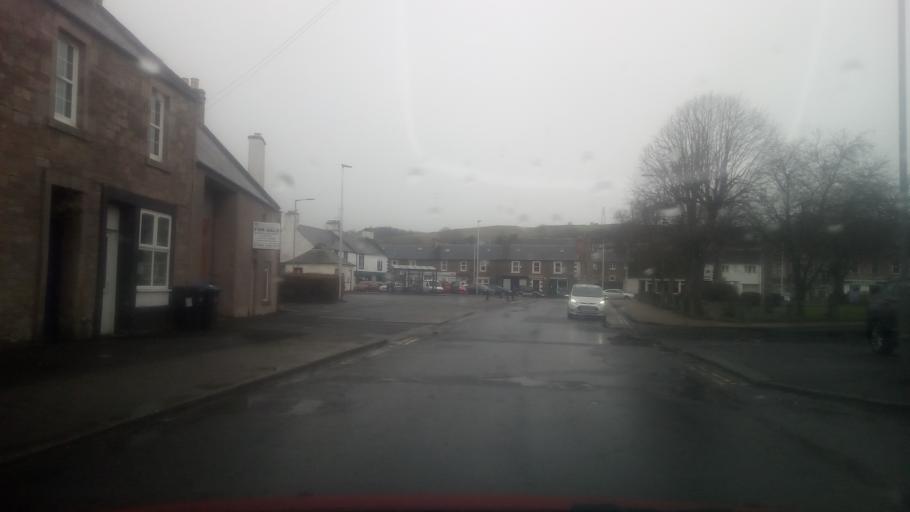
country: GB
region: Scotland
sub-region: The Scottish Borders
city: Earlston
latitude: 55.6376
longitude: -2.6767
